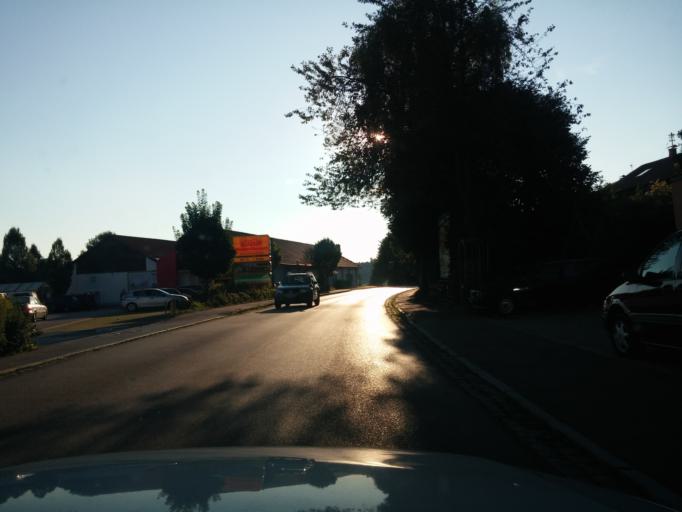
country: DE
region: Bavaria
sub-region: Swabia
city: Altusried
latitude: 47.8063
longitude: 10.2099
